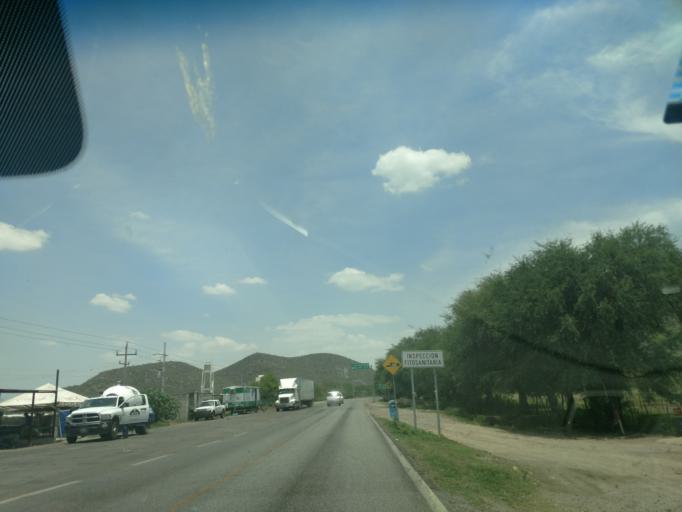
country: MX
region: San Luis Potosi
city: Ciudad Fernandez
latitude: 22.0059
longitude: -100.1484
